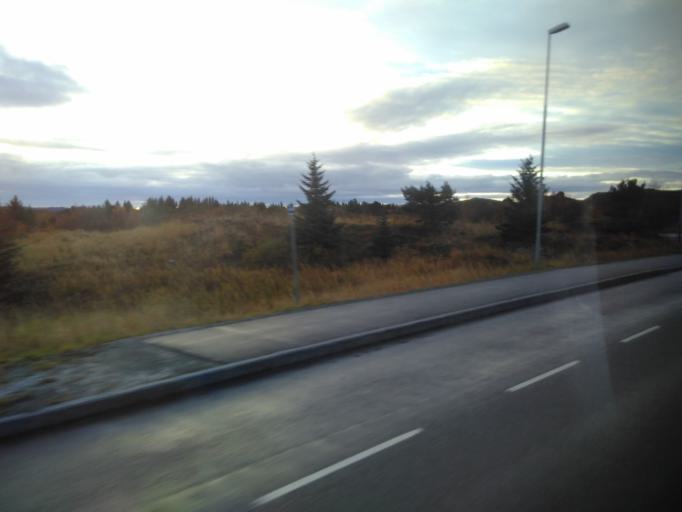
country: NO
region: Sor-Trondelag
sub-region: Froya
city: Sistranda
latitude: 63.6480
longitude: 8.8234
